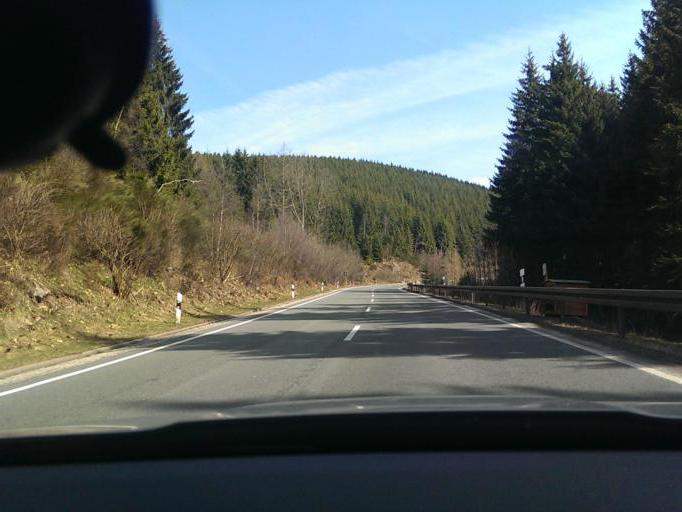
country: DE
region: Thuringia
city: Luisenthal
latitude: 50.7617
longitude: 10.7391
